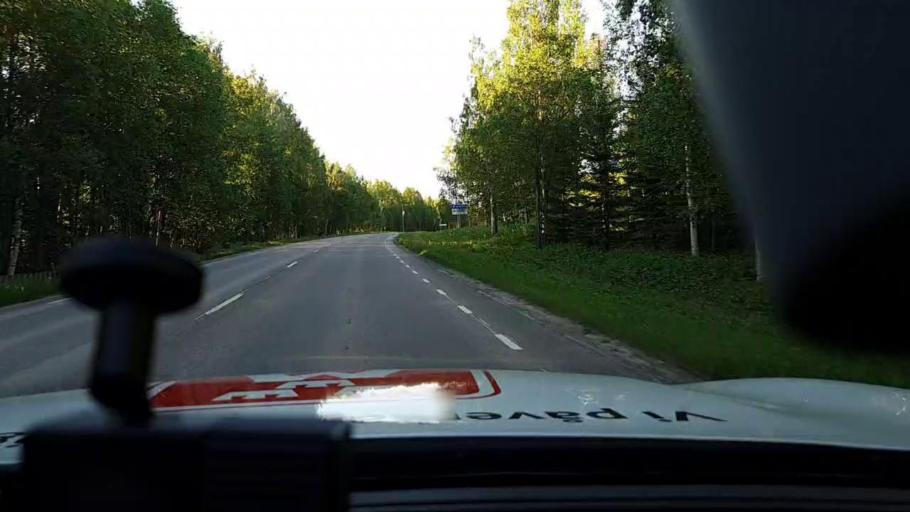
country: SE
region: Norrbotten
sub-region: Lulea Kommun
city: Lulea
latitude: 65.6099
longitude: 22.1883
